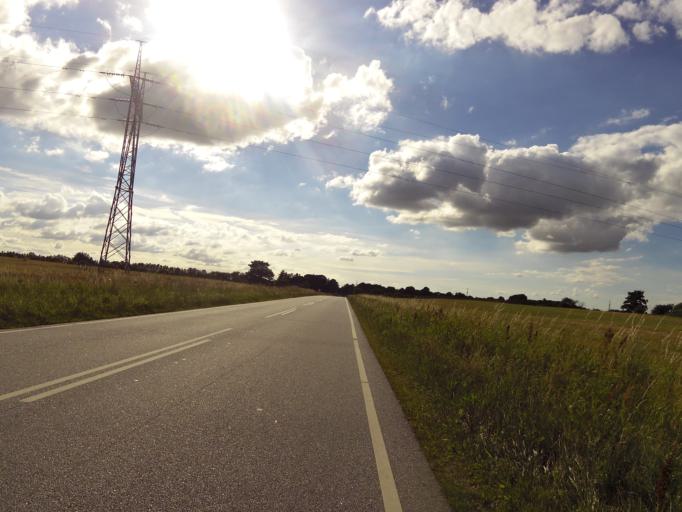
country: DK
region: South Denmark
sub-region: Haderslev Kommune
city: Vojens
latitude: 55.1958
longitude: 9.3454
